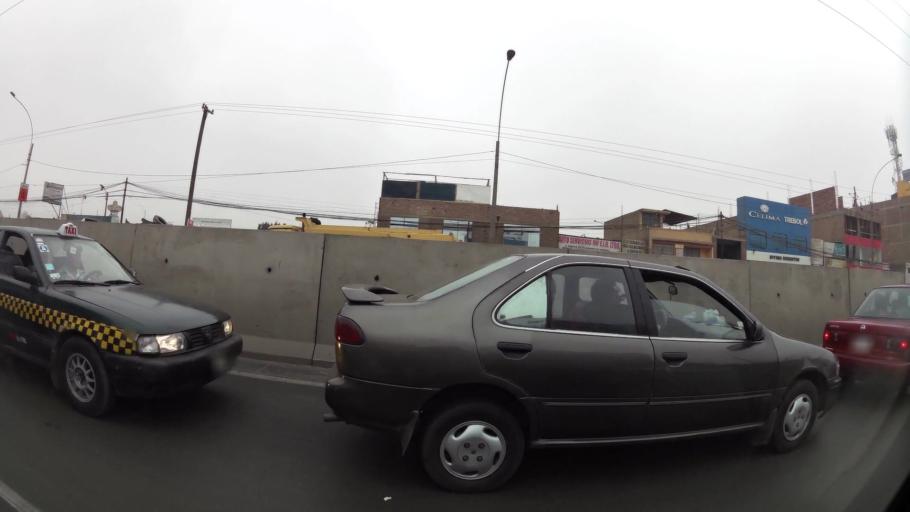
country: PE
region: Lima
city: Ventanilla
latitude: -11.8562
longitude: -77.0853
